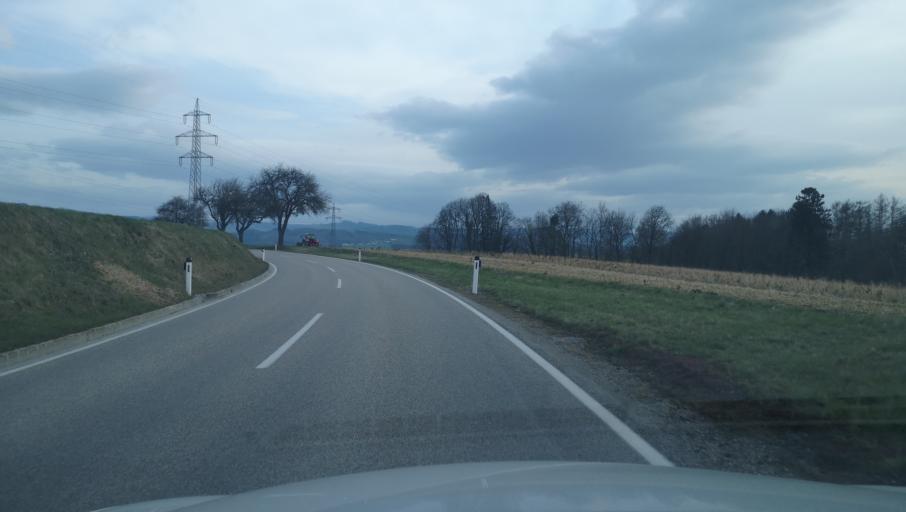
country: AT
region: Lower Austria
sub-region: Politischer Bezirk Amstetten
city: Winklarn
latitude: 48.0846
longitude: 14.8397
